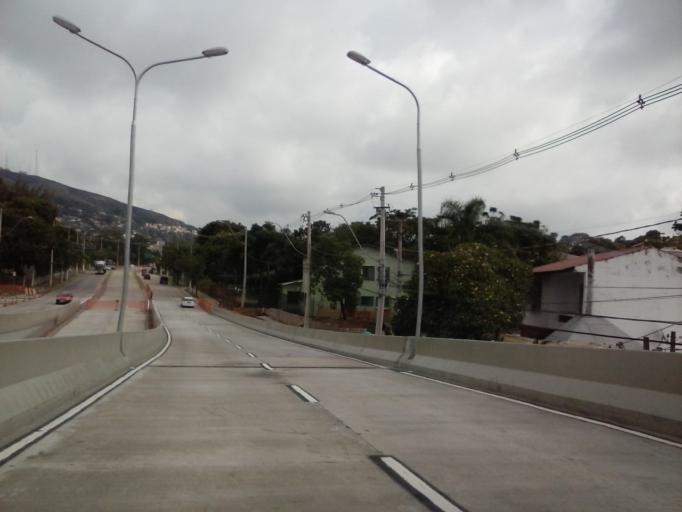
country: BR
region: Rio Grande do Sul
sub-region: Porto Alegre
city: Porto Alegre
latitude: -30.0645
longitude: -51.1864
